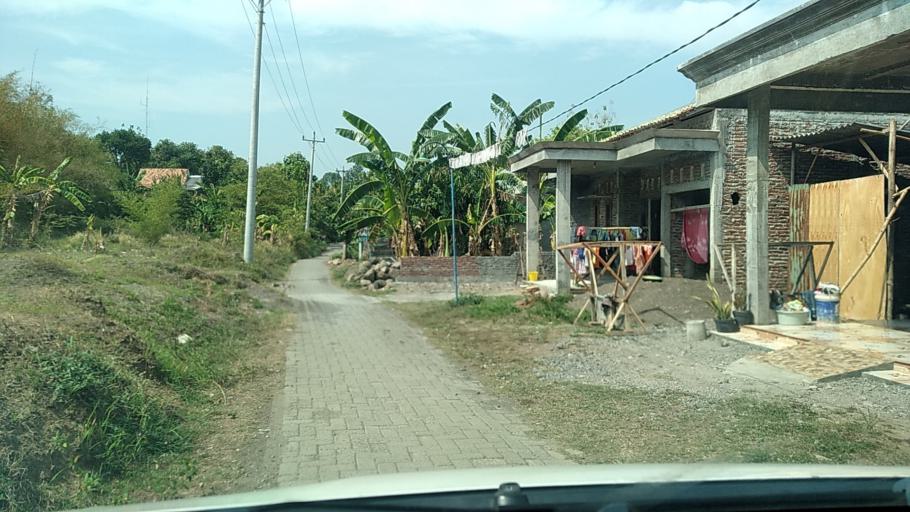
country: ID
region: Central Java
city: Mranggen
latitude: -7.0589
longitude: 110.4851
